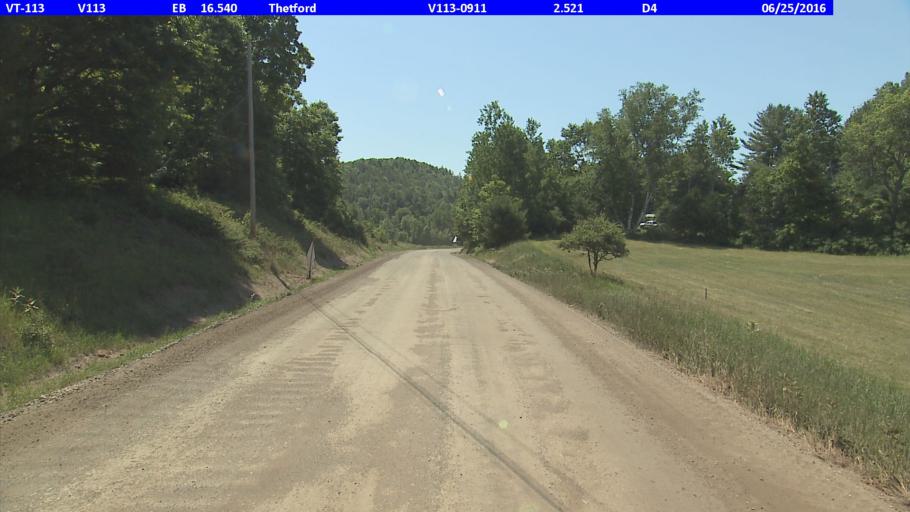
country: US
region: New Hampshire
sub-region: Grafton County
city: Lyme
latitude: 43.8625
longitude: -72.2608
